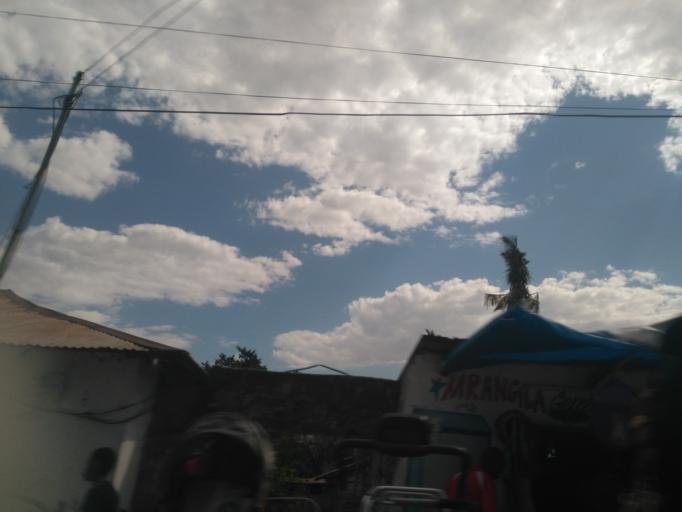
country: TZ
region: Mwanza
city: Mwanza
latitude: -2.5163
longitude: 32.9025
